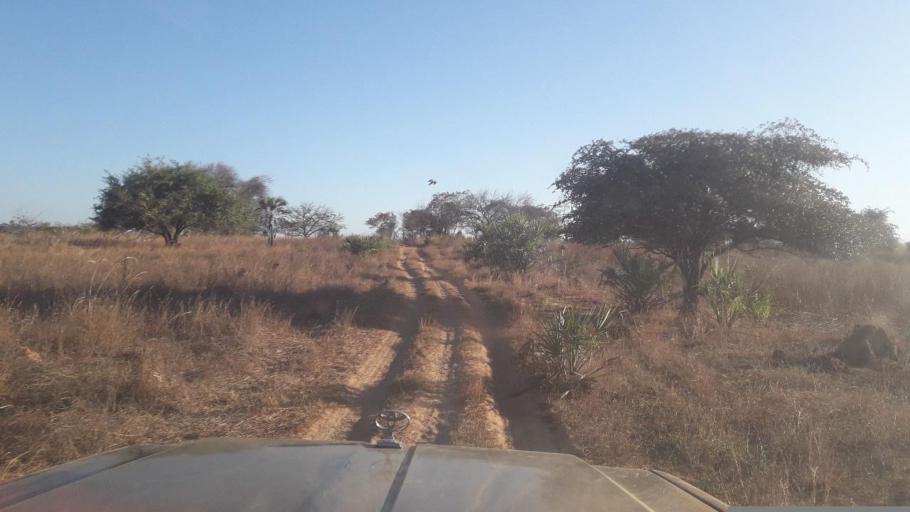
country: MG
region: Boeny
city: Sitampiky
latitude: -16.5023
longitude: 45.6026
